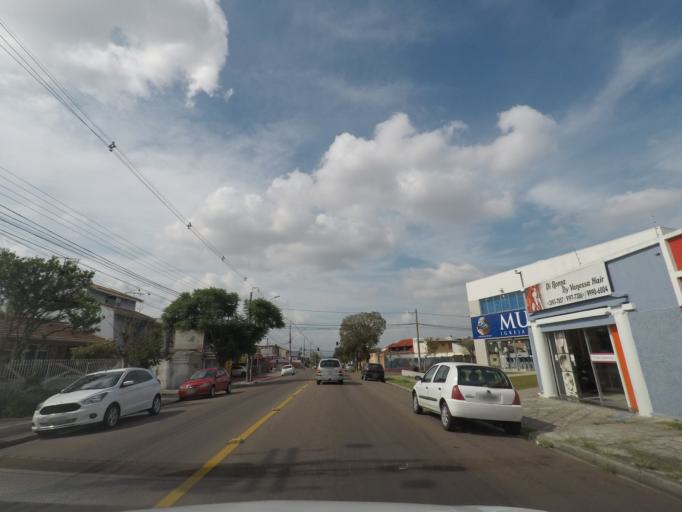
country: BR
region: Parana
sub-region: Pinhais
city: Pinhais
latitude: -25.4704
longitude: -49.2091
